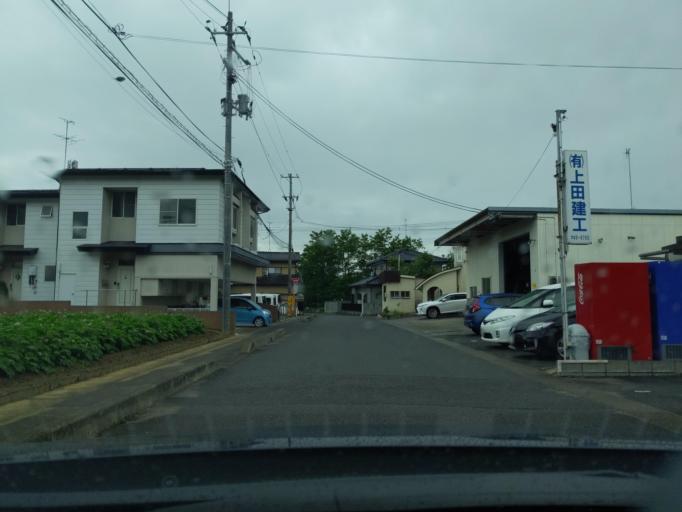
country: JP
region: Fukushima
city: Koriyama
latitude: 37.3671
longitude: 140.3567
